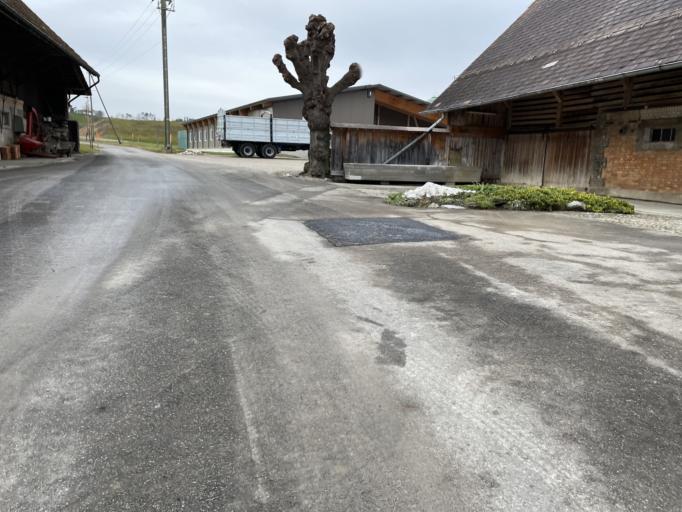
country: CH
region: Bern
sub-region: Bern-Mittelland District
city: Munsingen
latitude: 46.8675
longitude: 7.5327
